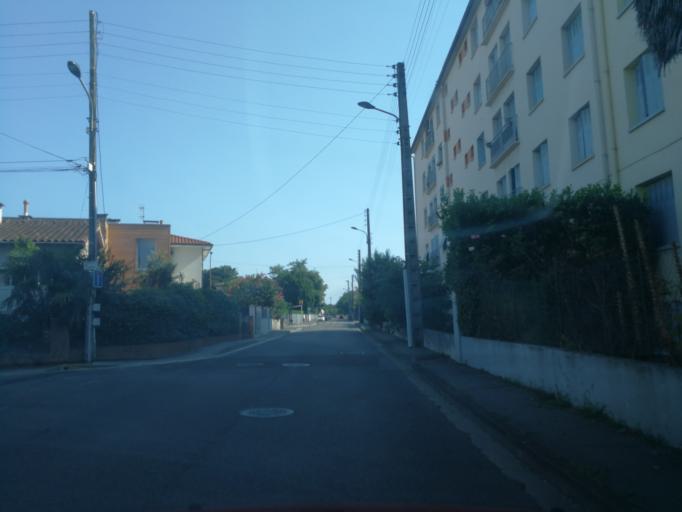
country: FR
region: Midi-Pyrenees
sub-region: Departement de la Haute-Garonne
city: Blagnac
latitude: 43.6197
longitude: 1.4081
